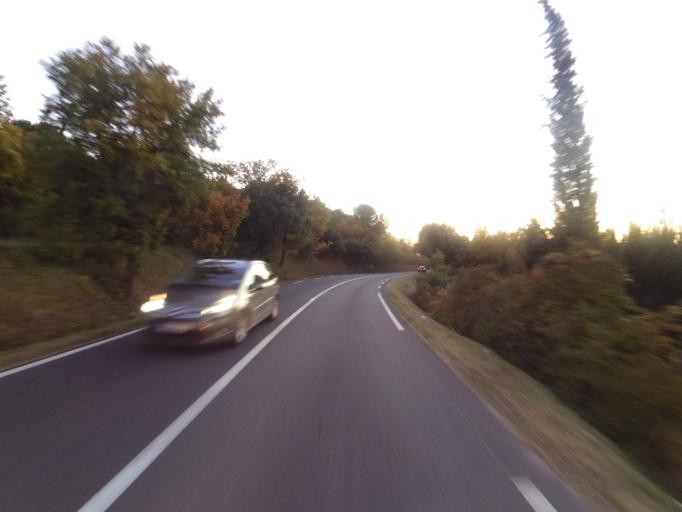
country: FR
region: Provence-Alpes-Cote d'Azur
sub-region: Departement du Vaucluse
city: Caromb
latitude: 44.1013
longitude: 5.1450
